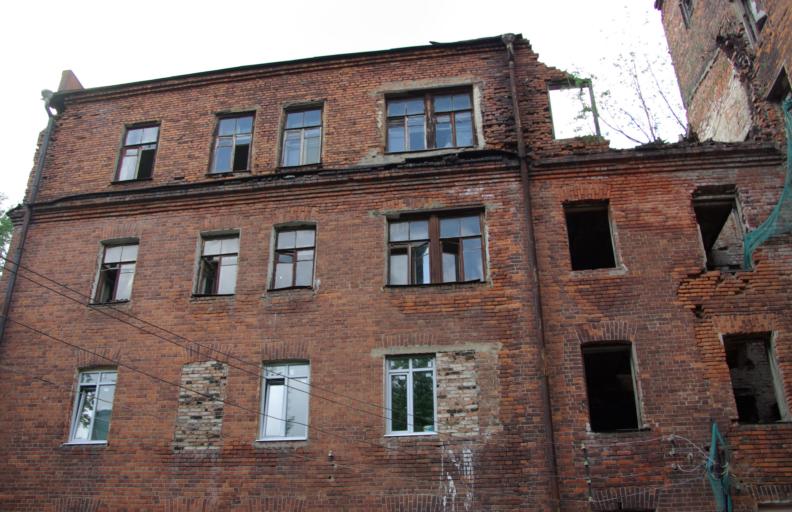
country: RU
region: Moscow
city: Kotlovka
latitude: 55.6814
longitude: 37.6126
